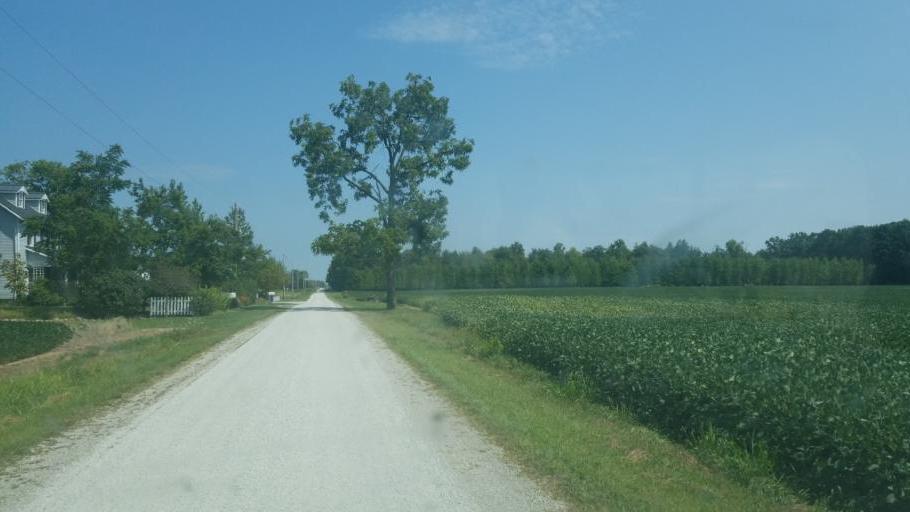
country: US
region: Ohio
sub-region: Crawford County
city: Bucyrus
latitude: 40.9359
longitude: -82.9252
